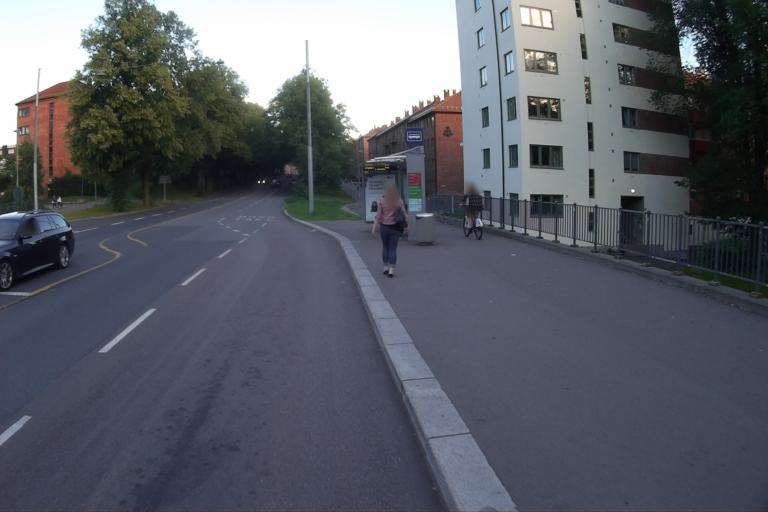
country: NO
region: Oslo
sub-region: Oslo
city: Oslo
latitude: 59.9293
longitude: 10.7693
